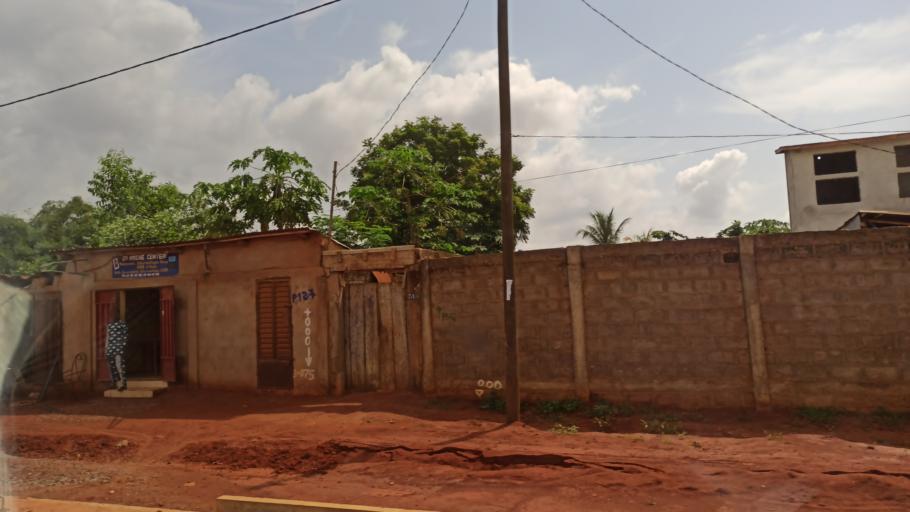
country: BJ
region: Queme
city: Porto-Novo
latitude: 6.4910
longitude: 2.5888
